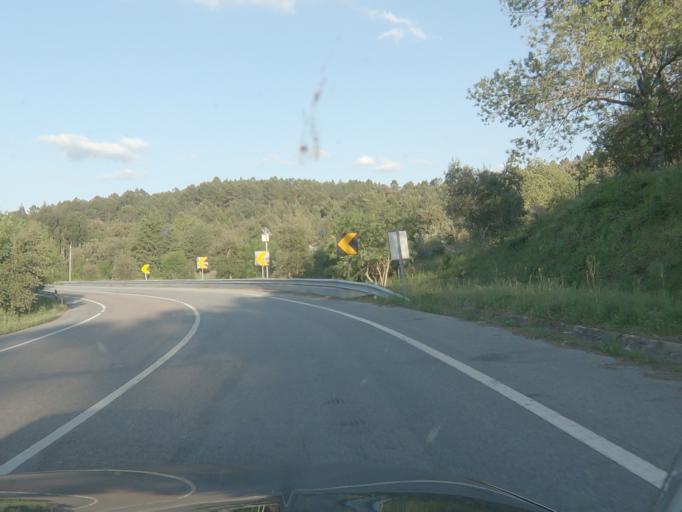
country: PT
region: Portalegre
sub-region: Marvao
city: Marvao
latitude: 39.3690
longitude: -7.3438
